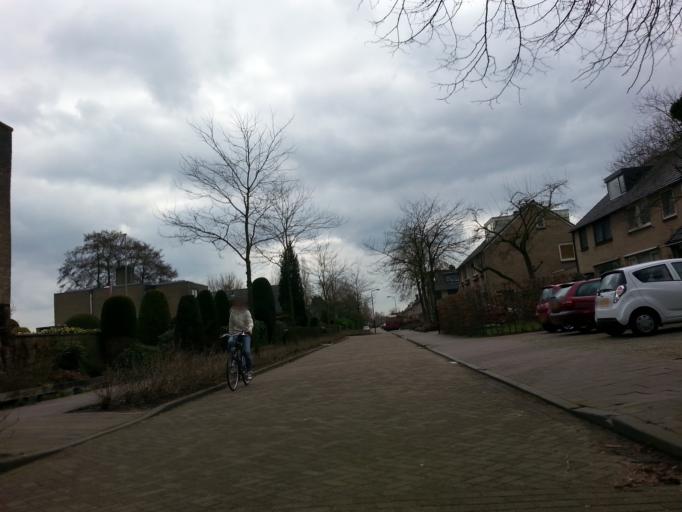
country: NL
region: Utrecht
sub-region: Gemeente Leusden
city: Leusden
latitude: 52.1176
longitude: 5.4076
